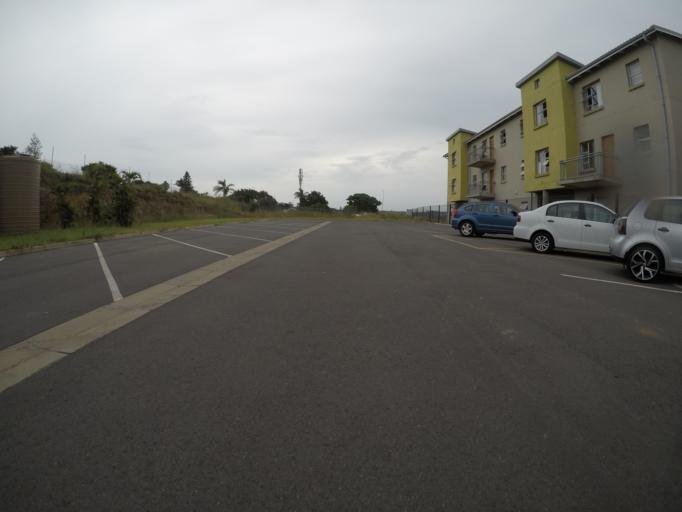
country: ZA
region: Eastern Cape
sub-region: Buffalo City Metropolitan Municipality
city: East London
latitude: -32.9950
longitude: 27.8541
